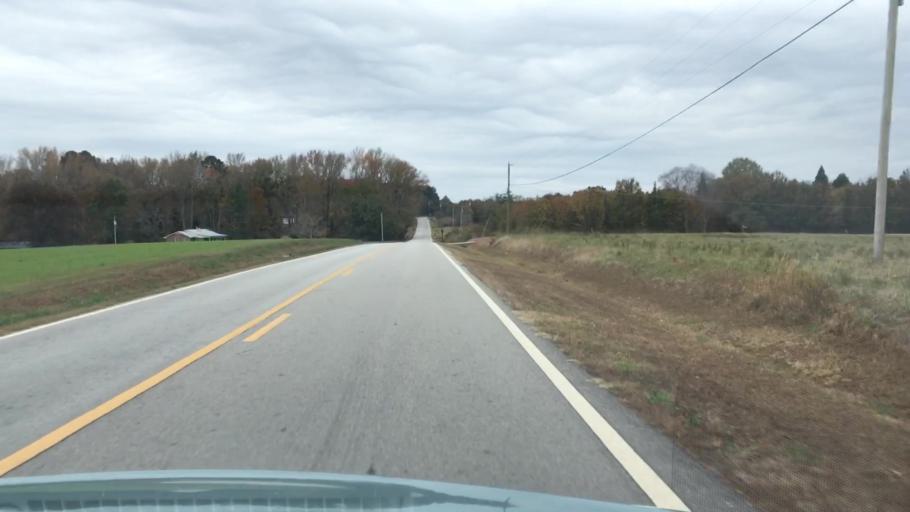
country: US
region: Georgia
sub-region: Henry County
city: McDonough
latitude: 33.5130
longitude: -84.1235
